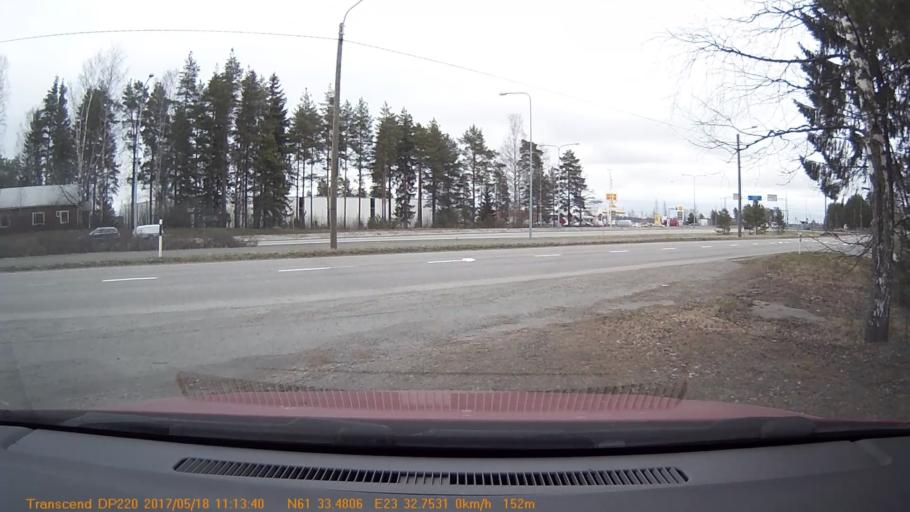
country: FI
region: Pirkanmaa
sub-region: Tampere
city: Yloejaervi
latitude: 61.5580
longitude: 23.5460
